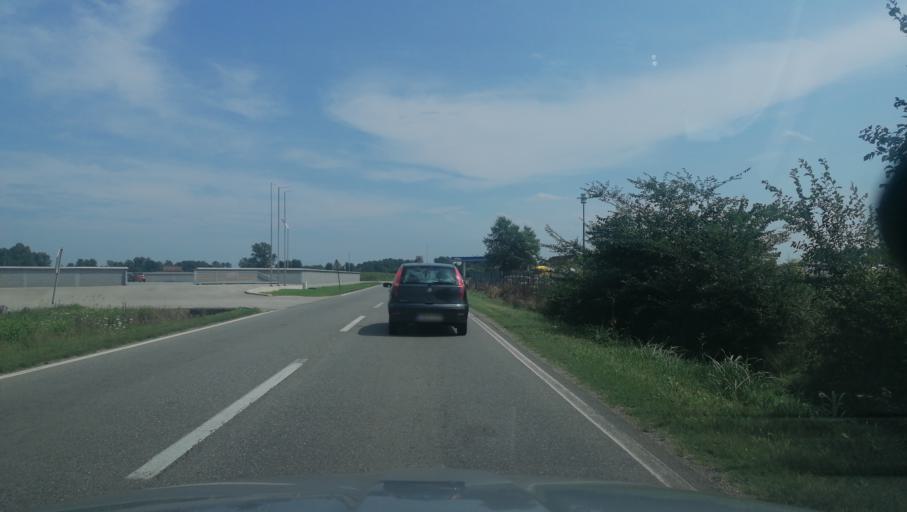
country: BA
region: Republika Srpska
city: Velika Obarska
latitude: 44.8268
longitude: 19.0332
